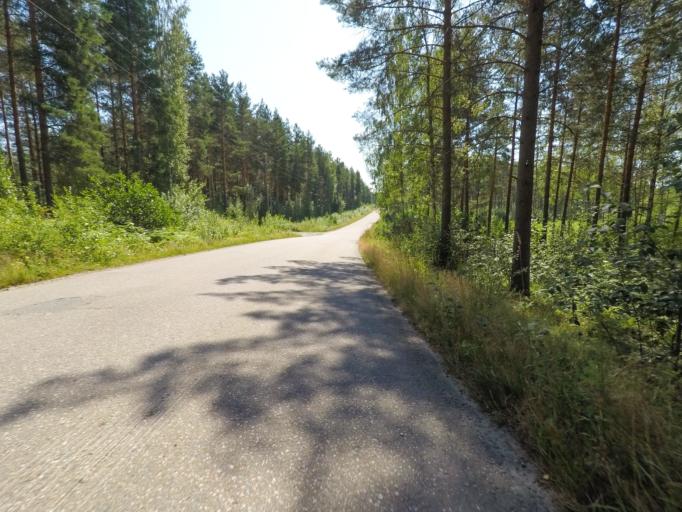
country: FI
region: Southern Savonia
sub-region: Mikkeli
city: Puumala
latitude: 61.4422
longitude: 28.1645
